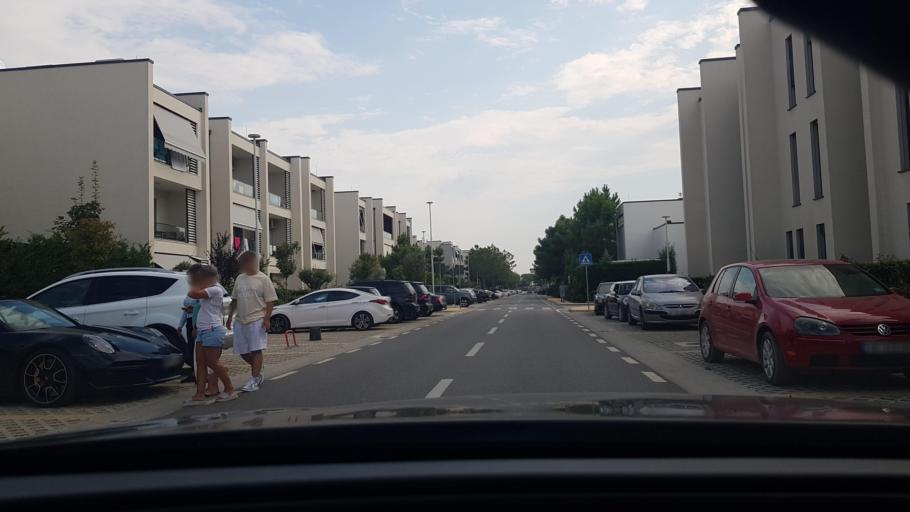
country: AL
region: Durres
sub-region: Rrethi i Durresit
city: Katundi i Ri
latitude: 41.4931
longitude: 19.5143
